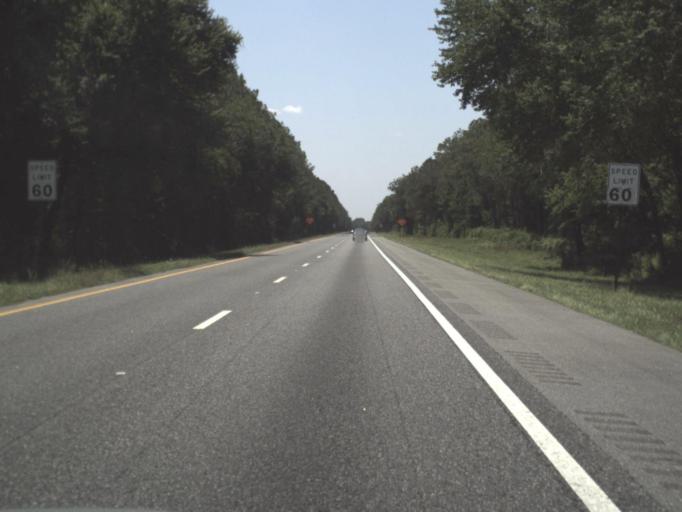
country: US
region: Florida
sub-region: Columbia County
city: Five Points
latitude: 30.2417
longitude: -82.5969
